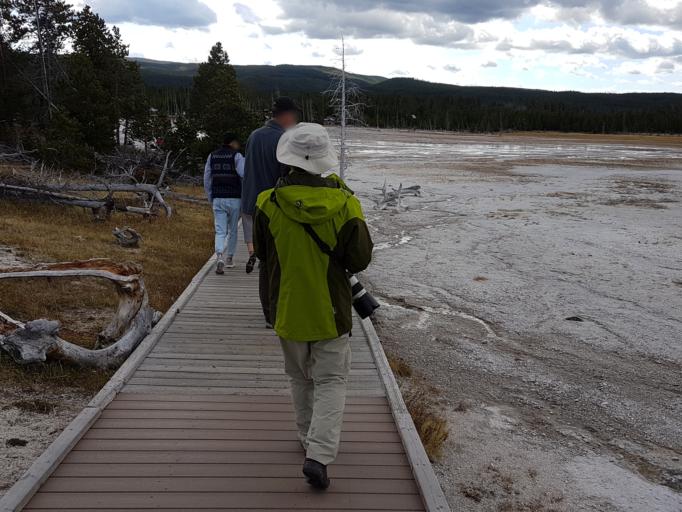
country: US
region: Montana
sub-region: Gallatin County
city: West Yellowstone
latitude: 44.5506
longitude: -110.8085
